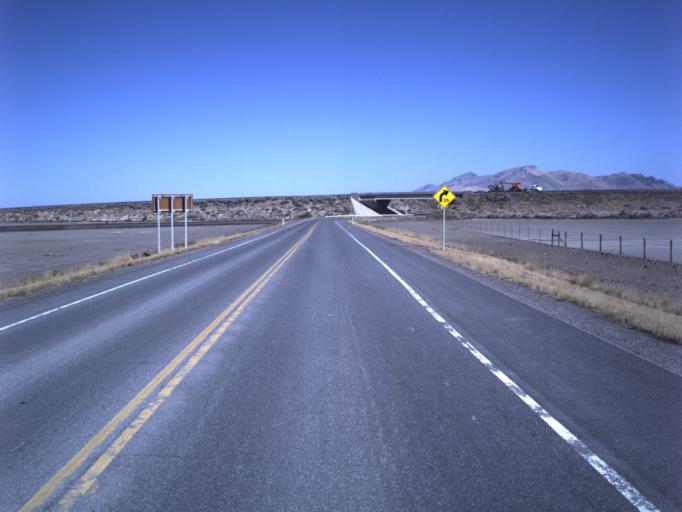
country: US
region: Utah
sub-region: Tooele County
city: Grantsville
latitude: 40.7061
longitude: -112.5301
